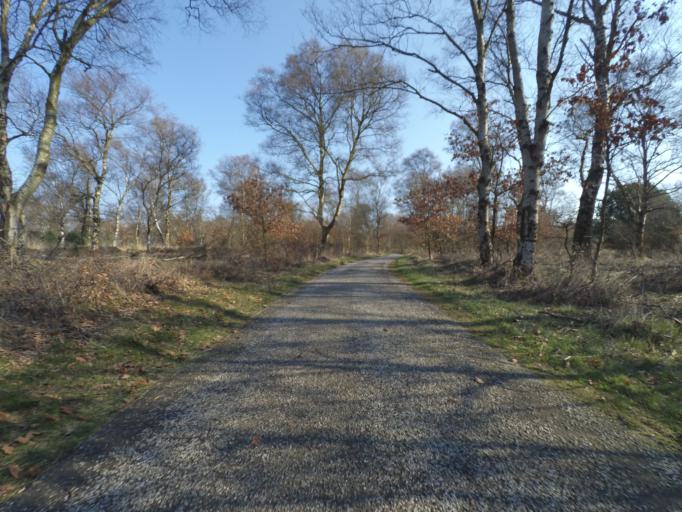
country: NL
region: Gelderland
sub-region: Gemeente Arnhem
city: Hoogkamp
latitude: 52.0569
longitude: 5.8512
